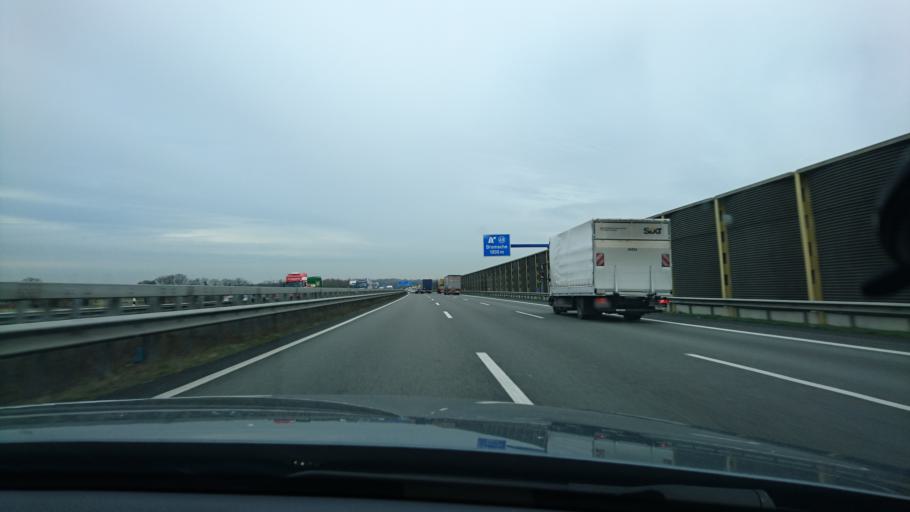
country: DE
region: Lower Saxony
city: Wallenhorst
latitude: 52.3803
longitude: 8.0436
